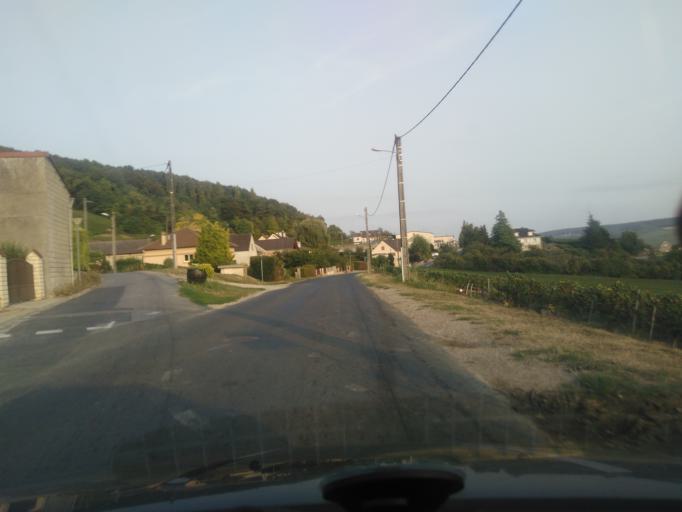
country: FR
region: Champagne-Ardenne
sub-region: Departement de la Marne
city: Damery
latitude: 49.0863
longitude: 3.8336
